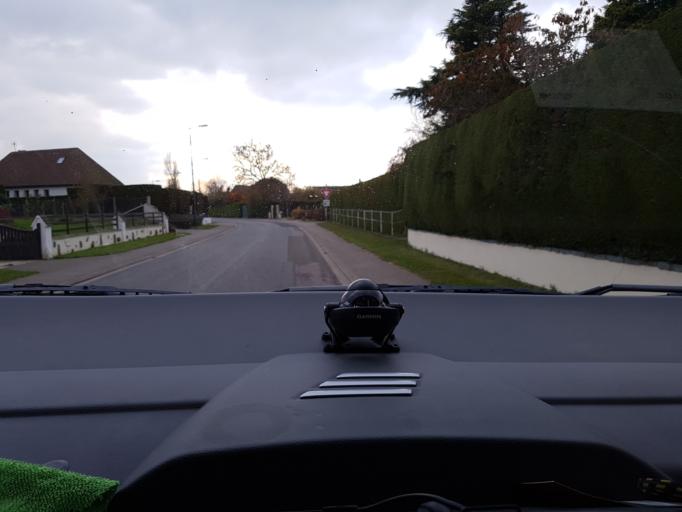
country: FR
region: Haute-Normandie
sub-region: Departement de la Seine-Maritime
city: Martin-Eglise
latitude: 49.9425
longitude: 1.1473
